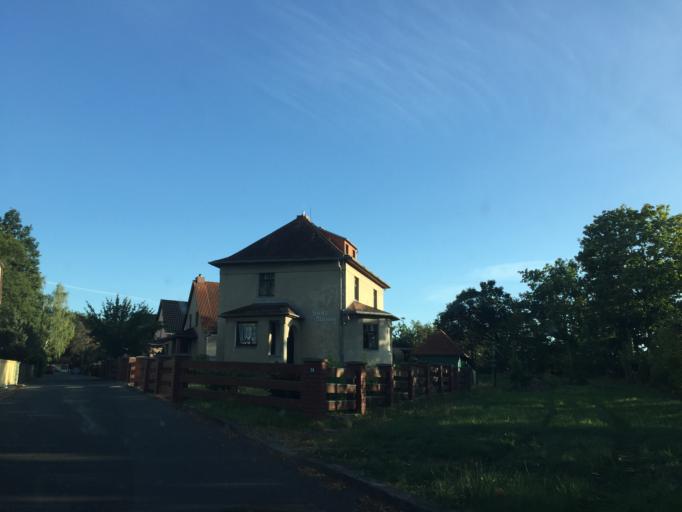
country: DE
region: Thuringia
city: Schmolln
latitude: 50.8942
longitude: 12.3544
